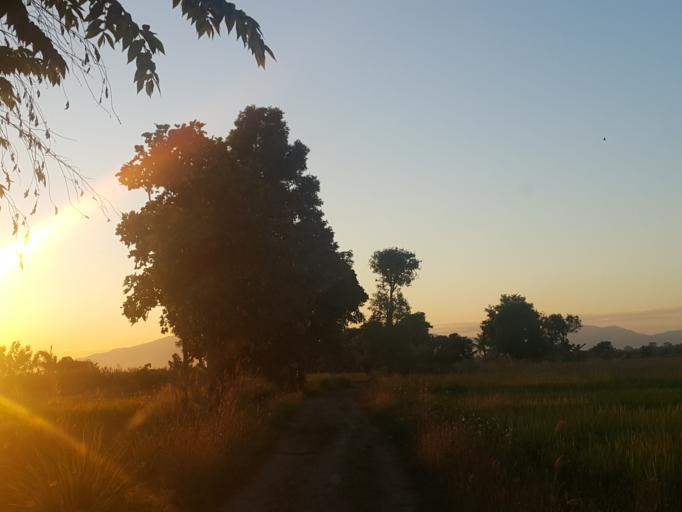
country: TH
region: Chiang Mai
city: San Kamphaeng
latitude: 18.8311
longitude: 99.1491
